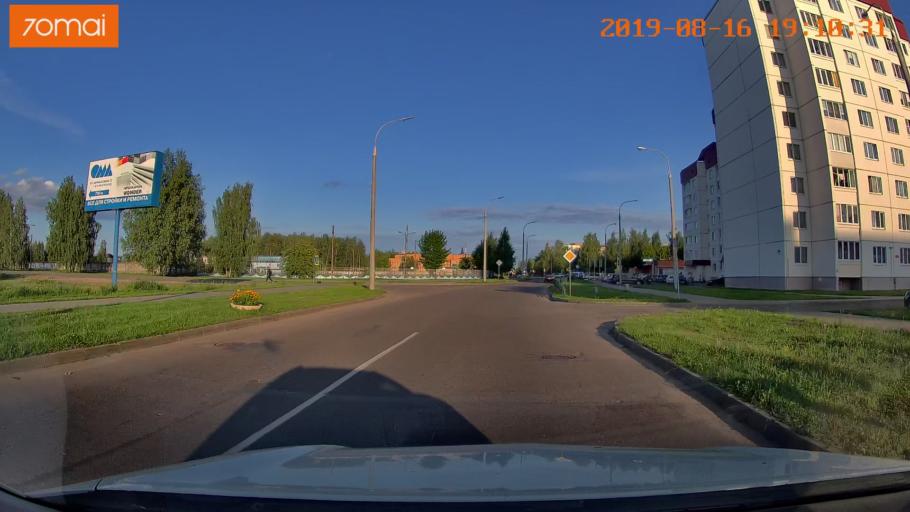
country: BY
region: Mogilev
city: Asipovichy
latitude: 53.3237
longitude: 28.6415
